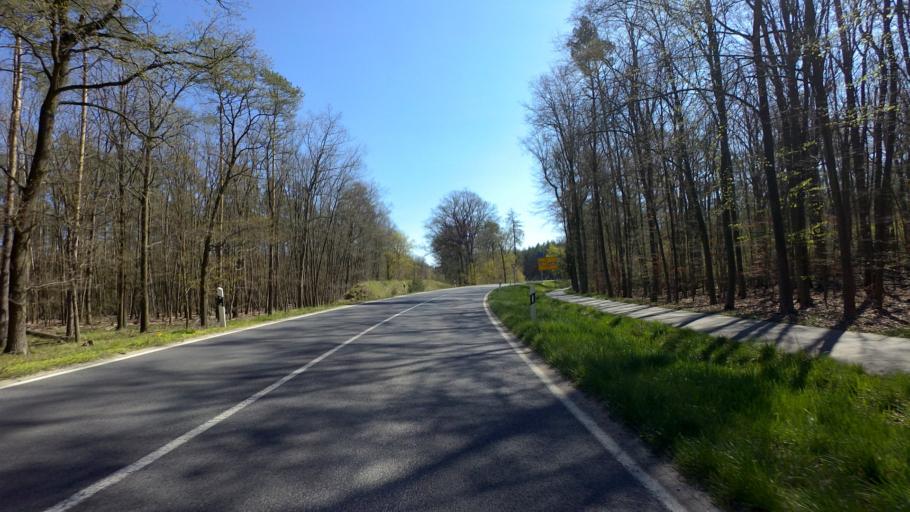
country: DE
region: Brandenburg
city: Schulzendorf
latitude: 52.3422
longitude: 13.5627
